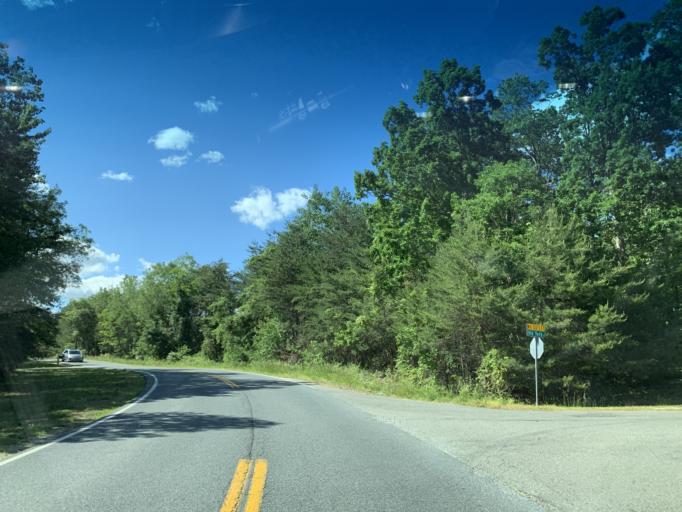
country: US
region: Maryland
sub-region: Cecil County
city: North East
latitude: 39.5563
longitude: -75.9243
